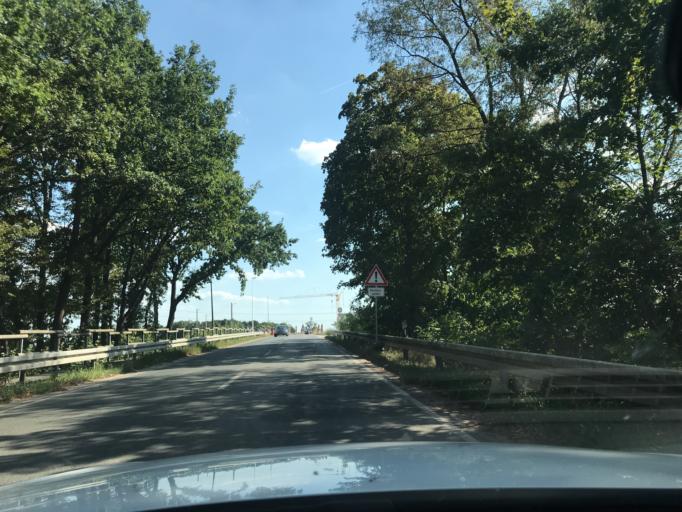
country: DE
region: Bavaria
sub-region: Regierungsbezirk Mittelfranken
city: Erlangen
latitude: 49.5622
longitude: 10.9866
